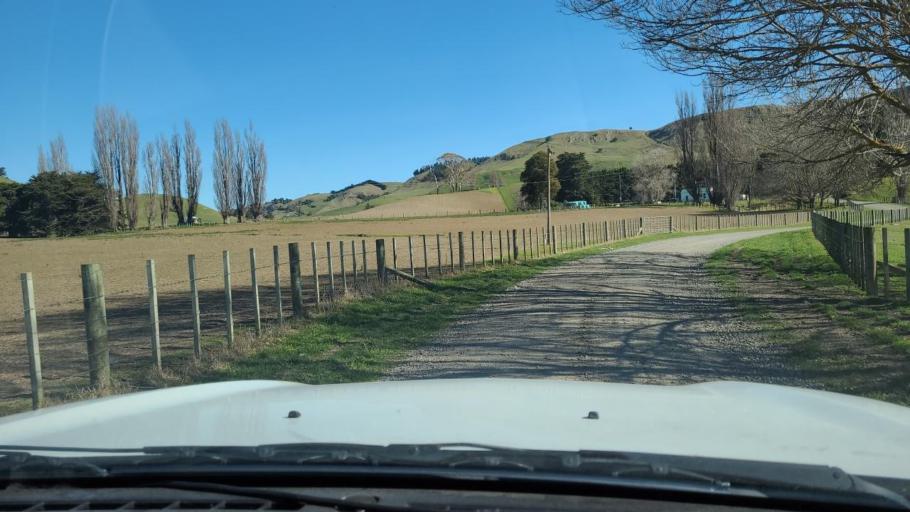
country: NZ
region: Hawke's Bay
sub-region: Hastings District
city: Hastings
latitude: -39.7949
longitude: 176.6431
